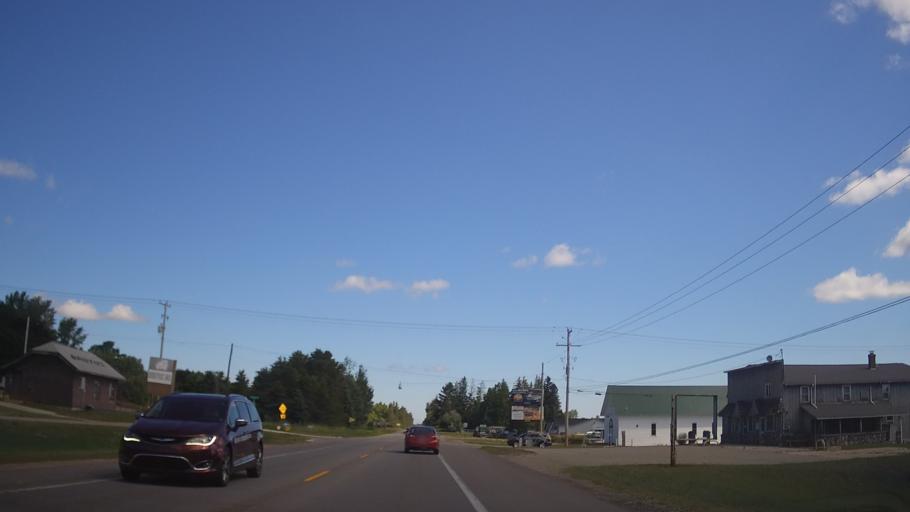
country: US
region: Michigan
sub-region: Cheboygan County
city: Indian River
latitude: 45.4926
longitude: -84.7812
